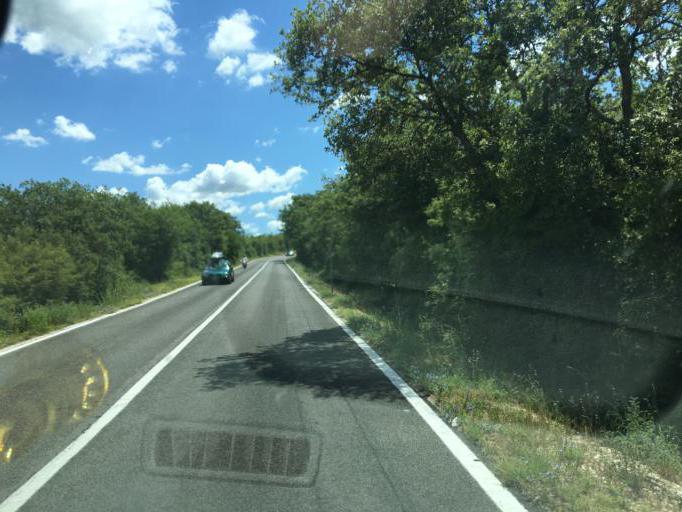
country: HR
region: Istarska
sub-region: Grad Rovinj
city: Rovinj
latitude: 45.1178
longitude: 13.7642
